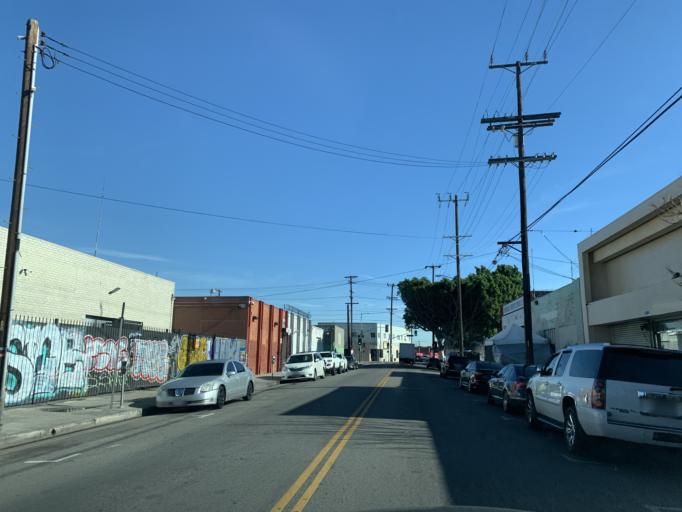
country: US
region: California
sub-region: Los Angeles County
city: Los Angeles
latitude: 34.0307
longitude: -118.2464
